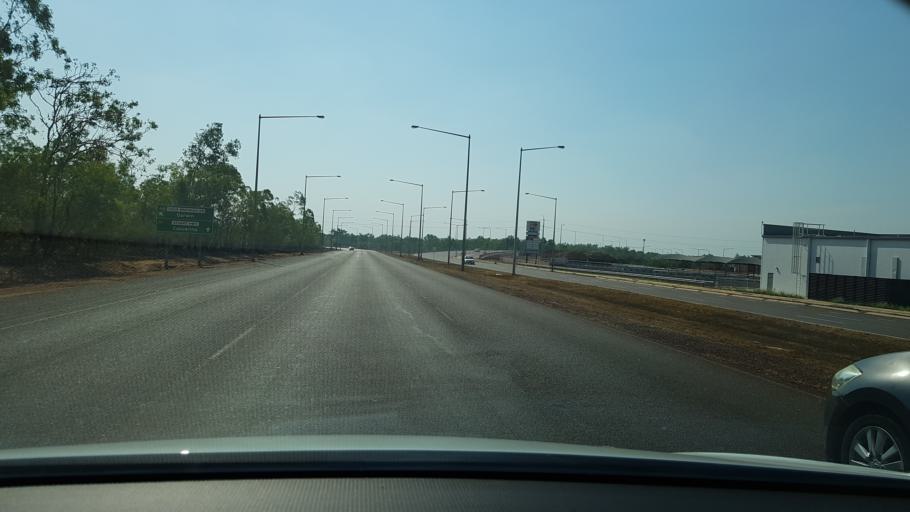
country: AU
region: Northern Territory
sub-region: Palmerston
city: Palmerston
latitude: -12.4703
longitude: 130.9802
